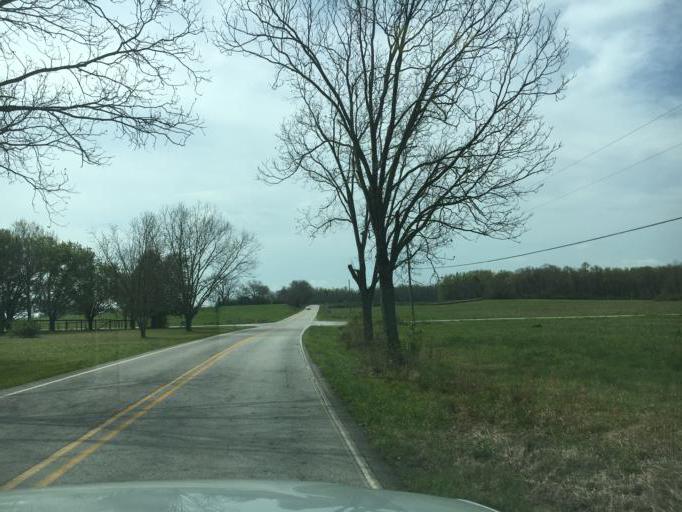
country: US
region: Georgia
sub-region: Hart County
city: Royston
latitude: 34.3364
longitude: -83.0387
